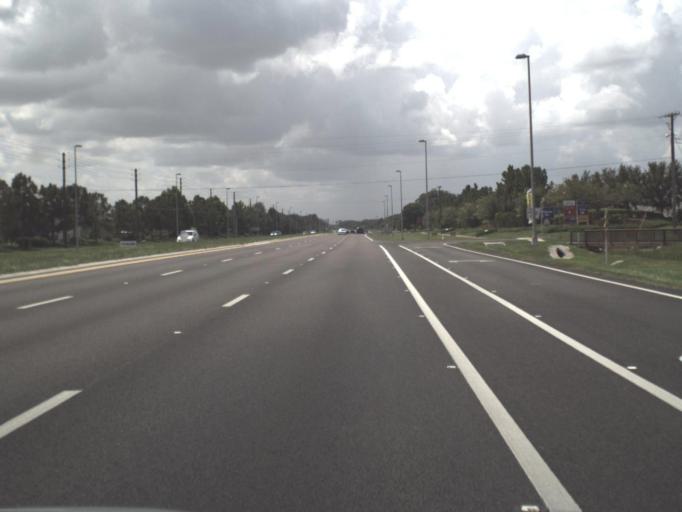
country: US
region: Florida
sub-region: Hillsborough County
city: Riverview
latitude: 27.8112
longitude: -82.3331
